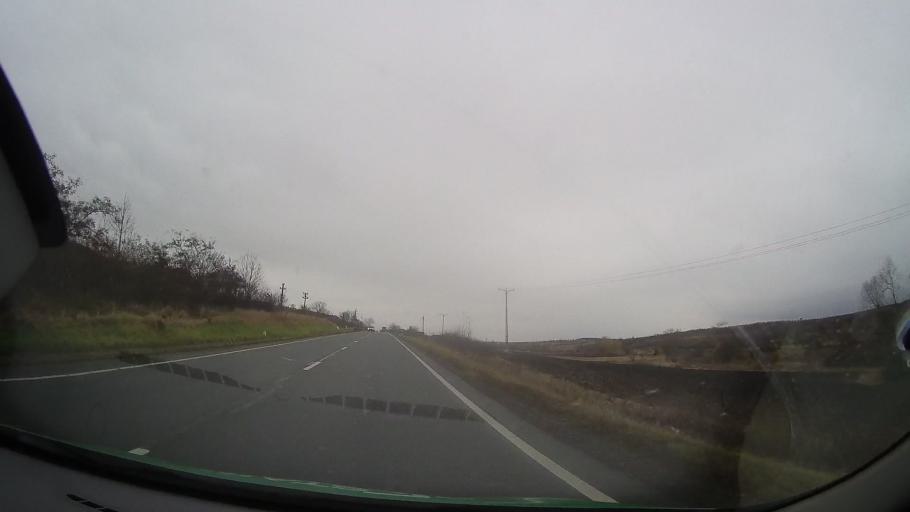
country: RO
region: Mures
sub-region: Comuna Breaza
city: Breaza
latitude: 46.7774
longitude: 24.6559
